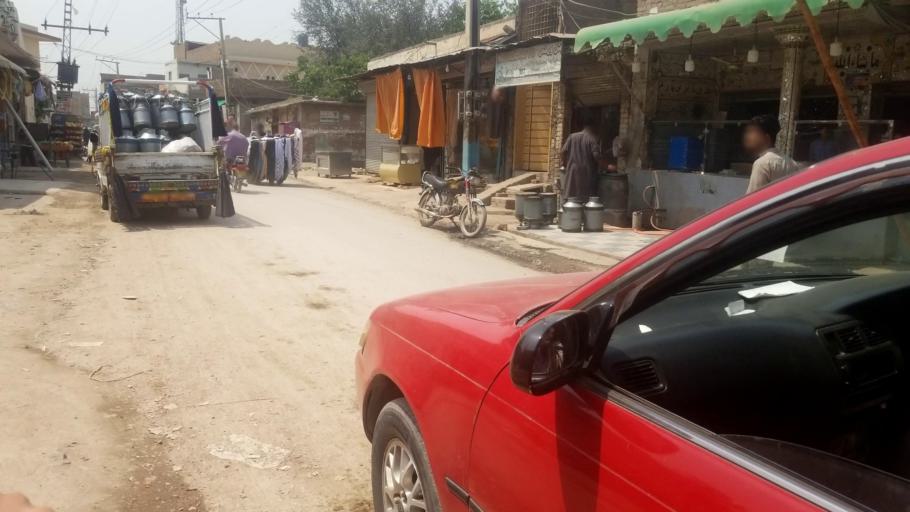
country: PK
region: Khyber Pakhtunkhwa
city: Peshawar
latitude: 34.0262
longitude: 71.6230
